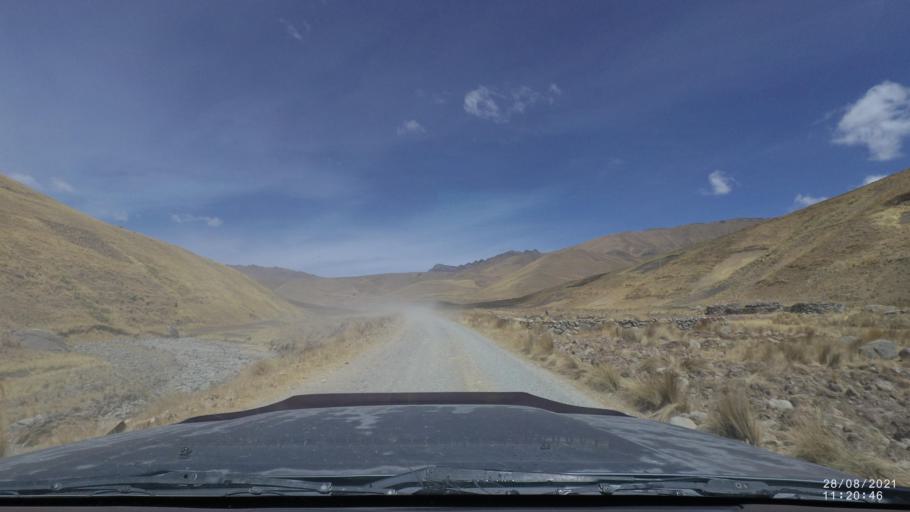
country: BO
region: Cochabamba
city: Sipe Sipe
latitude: -17.1607
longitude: -66.3428
